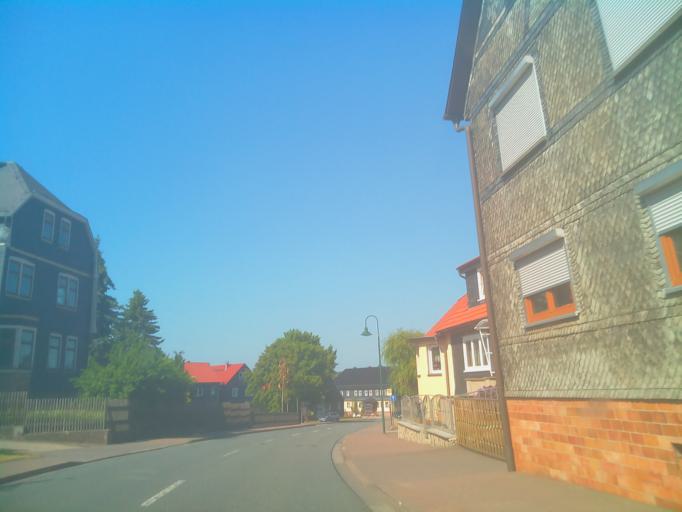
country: DE
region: Thuringia
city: Pennewitz
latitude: 50.6625
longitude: 11.0707
